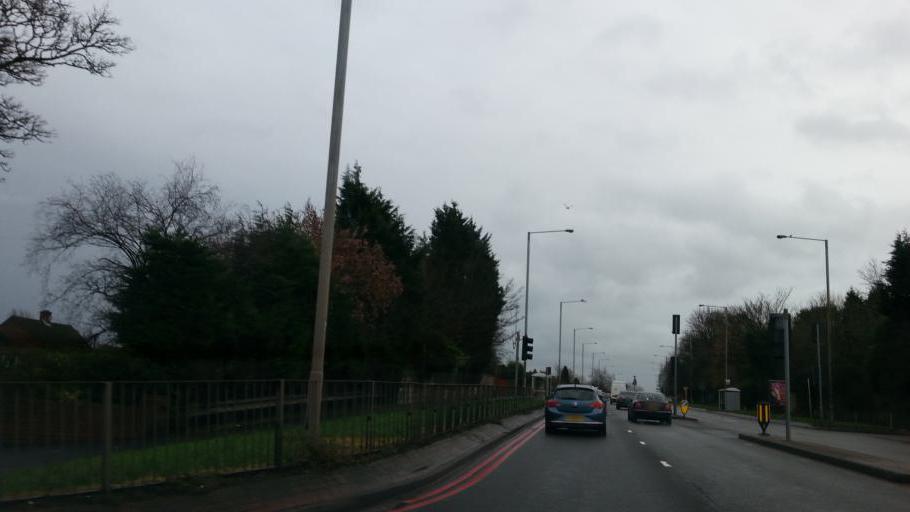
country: GB
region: England
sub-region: Sandwell
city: Oldbury
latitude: 52.5079
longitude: -2.0398
